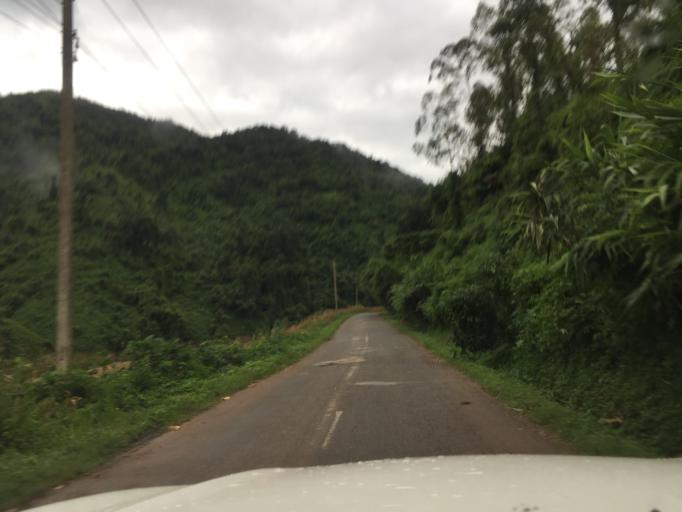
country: LA
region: Oudomxai
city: Muang La
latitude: 20.9524
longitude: 102.2144
